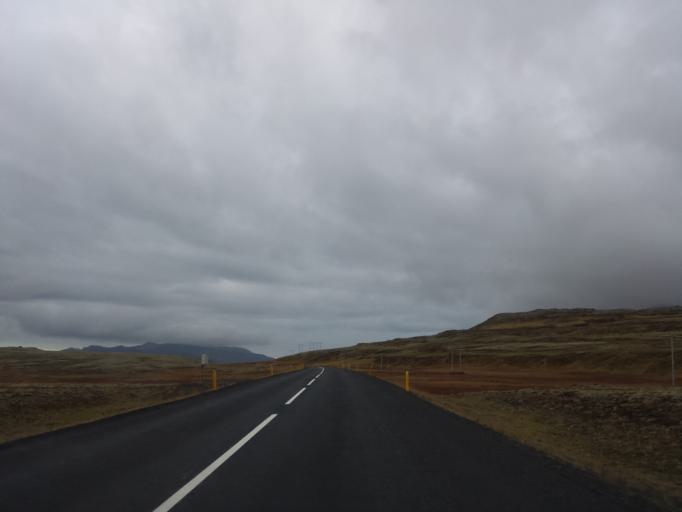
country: IS
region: West
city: Stykkisholmur
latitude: 64.9093
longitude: -22.8641
